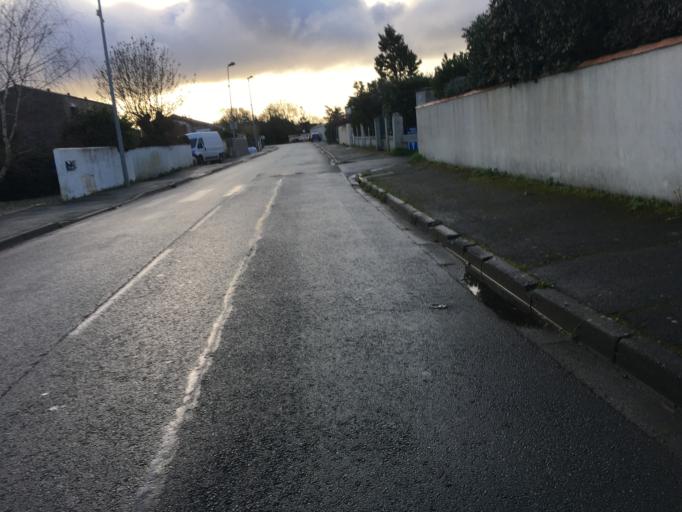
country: FR
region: Poitou-Charentes
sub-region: Departement de la Charente-Maritime
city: Nieul-sur-Mer
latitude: 46.1909
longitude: -1.1849
